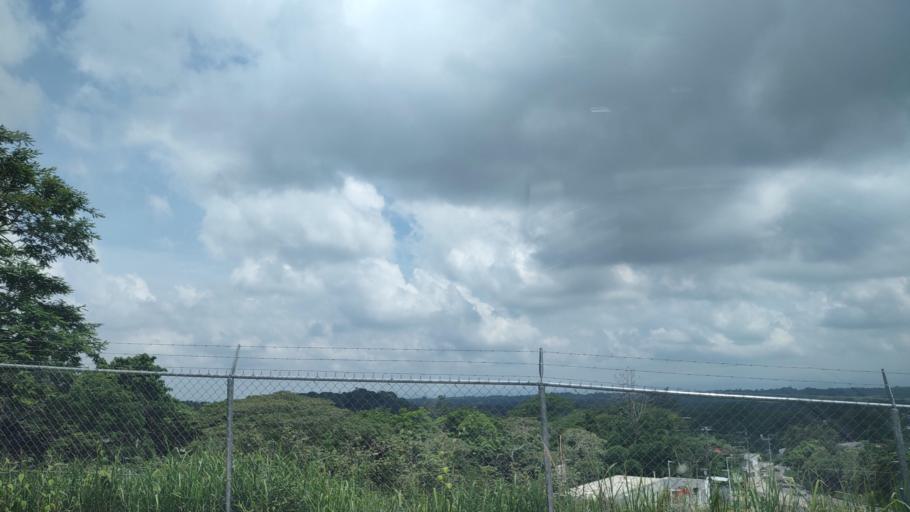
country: MX
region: Veracruz
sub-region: Emiliano Zapata
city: Jacarandas
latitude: 19.4706
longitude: -96.8496
